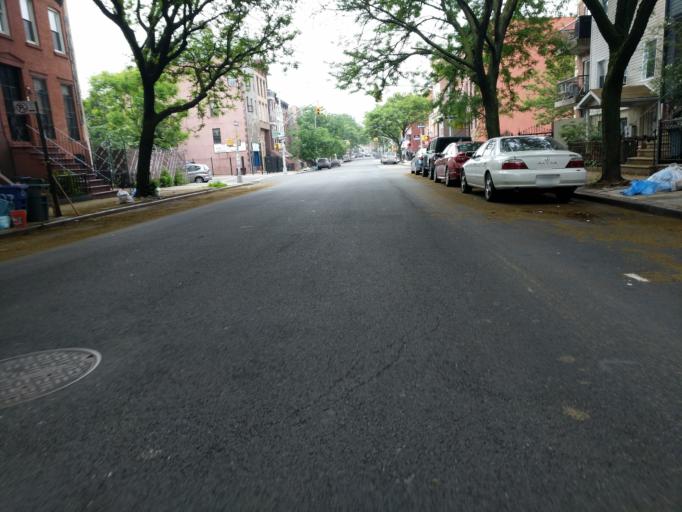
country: US
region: New York
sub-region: Kings County
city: Brooklyn
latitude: 40.6846
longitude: -73.9564
